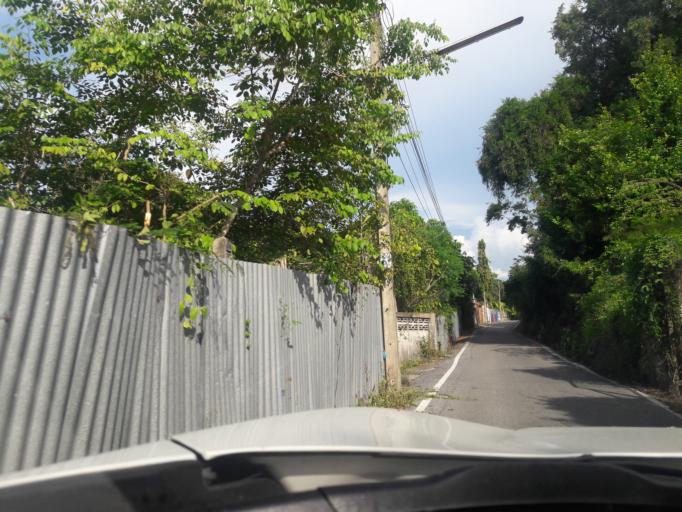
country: TH
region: Lop Buri
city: Ban Mi
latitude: 15.0469
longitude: 100.5484
